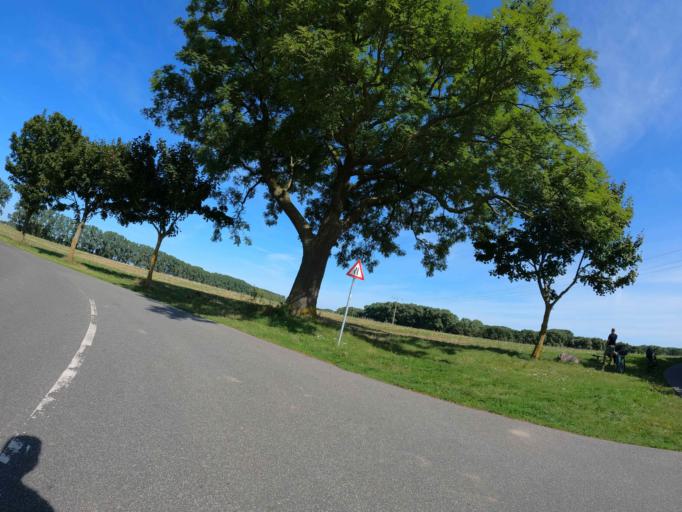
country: DE
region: Mecklenburg-Vorpommern
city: Kramerhof
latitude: 54.3606
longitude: 13.0637
